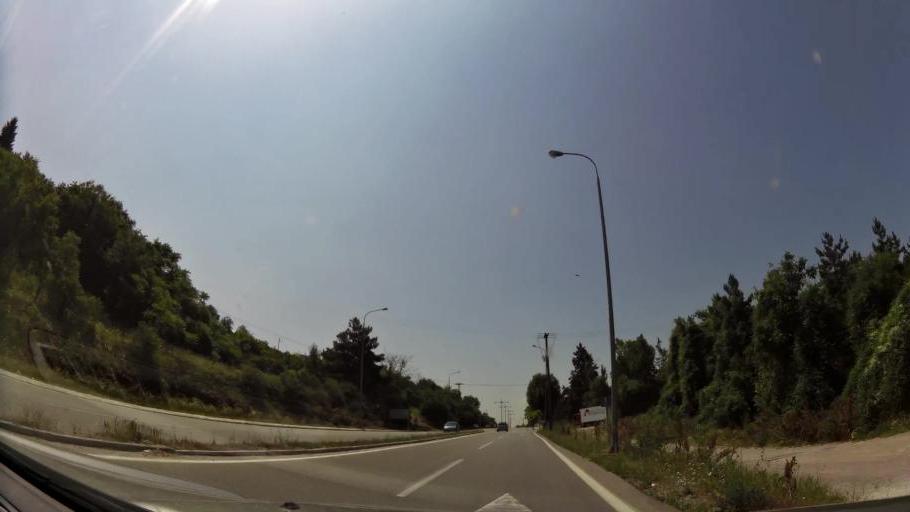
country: GR
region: West Macedonia
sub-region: Nomos Kozanis
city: Kozani
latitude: 40.3123
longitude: 21.7840
